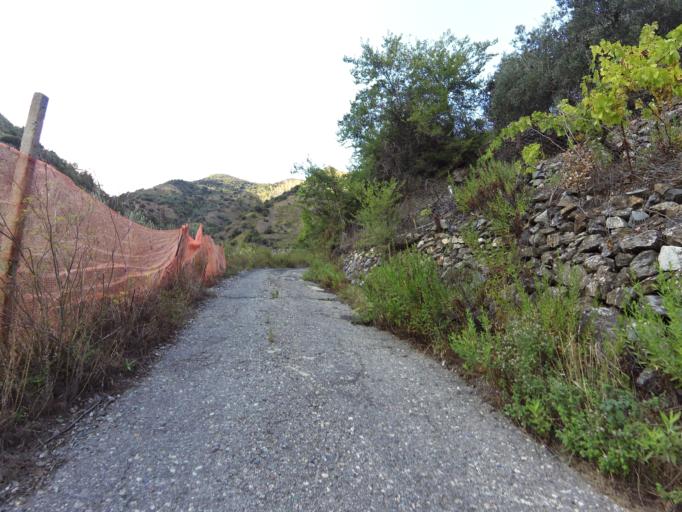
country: IT
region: Calabria
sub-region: Provincia di Reggio Calabria
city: Bivongi
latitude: 38.4911
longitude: 16.4556
